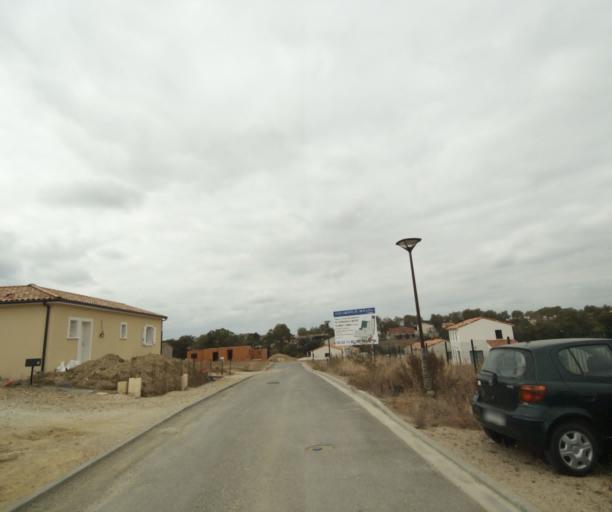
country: FR
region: Midi-Pyrenees
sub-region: Departement de la Haute-Garonne
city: Villefranche-de-Lauragais
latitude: 43.4052
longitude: 1.7211
